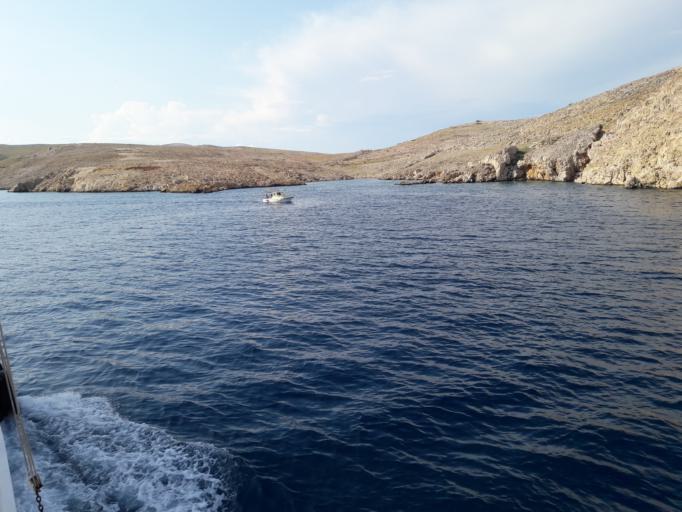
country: HR
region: Primorsko-Goranska
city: Banjol
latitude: 44.7048
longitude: 14.8655
